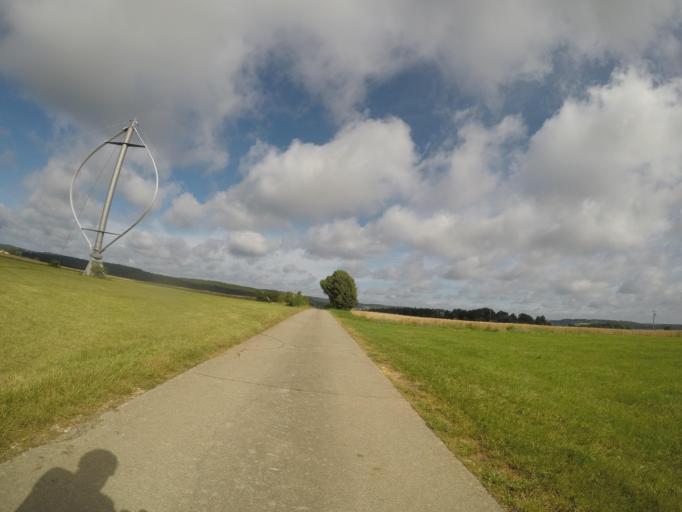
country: DE
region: Baden-Wuerttemberg
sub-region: Tuebingen Region
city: Laichingen
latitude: 48.4472
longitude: 9.6388
